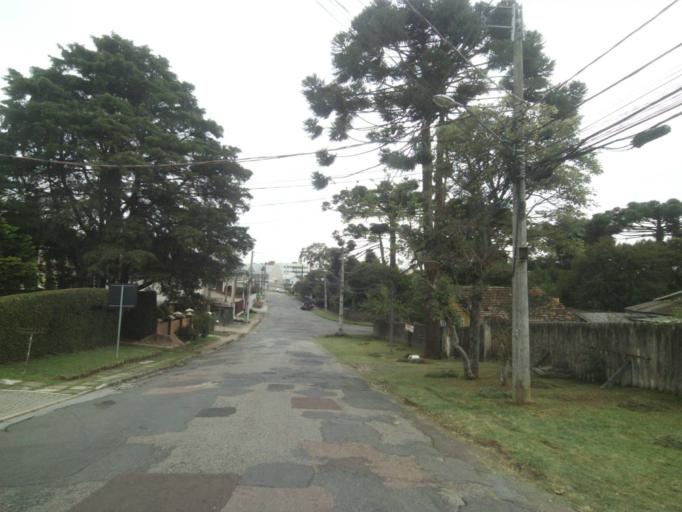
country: BR
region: Parana
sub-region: Curitiba
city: Curitiba
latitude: -25.4057
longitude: -49.2931
